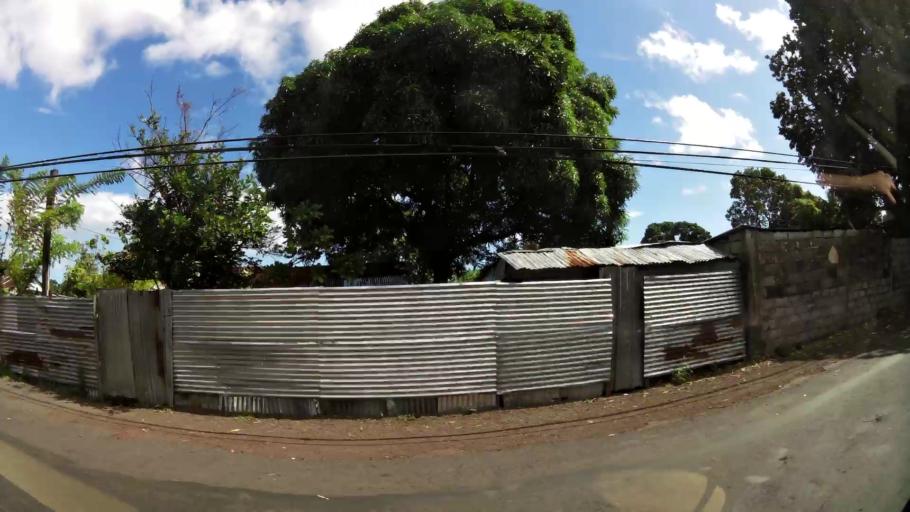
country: KM
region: Grande Comore
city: Mavingouni
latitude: -11.7339
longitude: 43.2496
